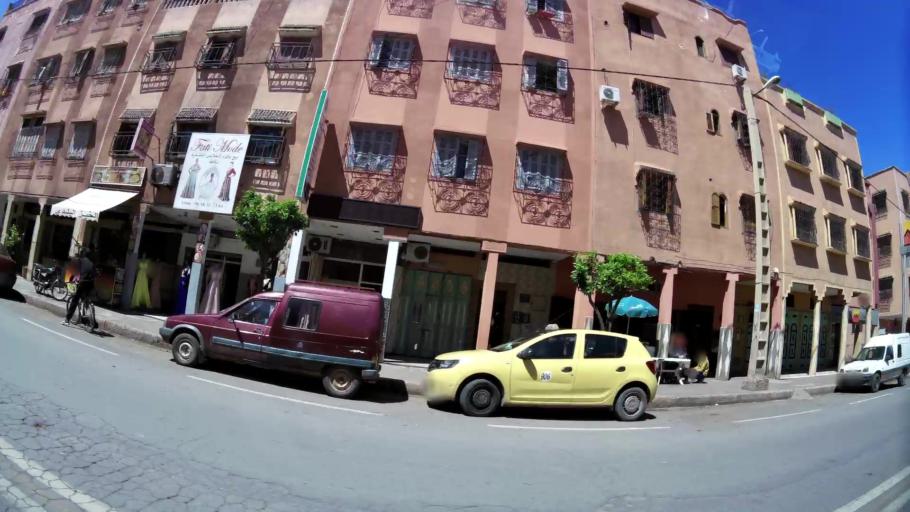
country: MA
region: Marrakech-Tensift-Al Haouz
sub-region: Marrakech
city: Marrakesh
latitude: 31.6334
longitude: -8.0678
